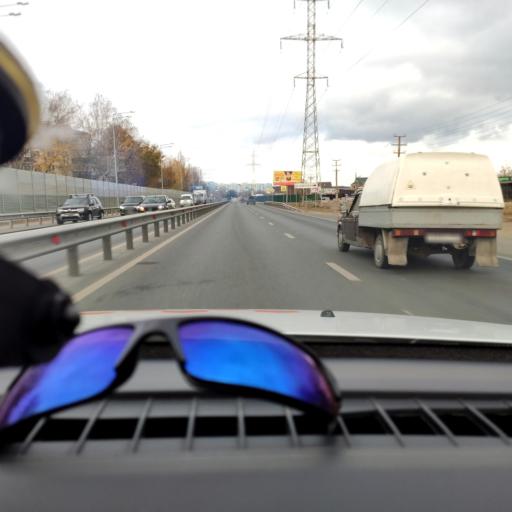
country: RU
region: Samara
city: Novosemeykino
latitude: 53.3499
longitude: 50.2292
